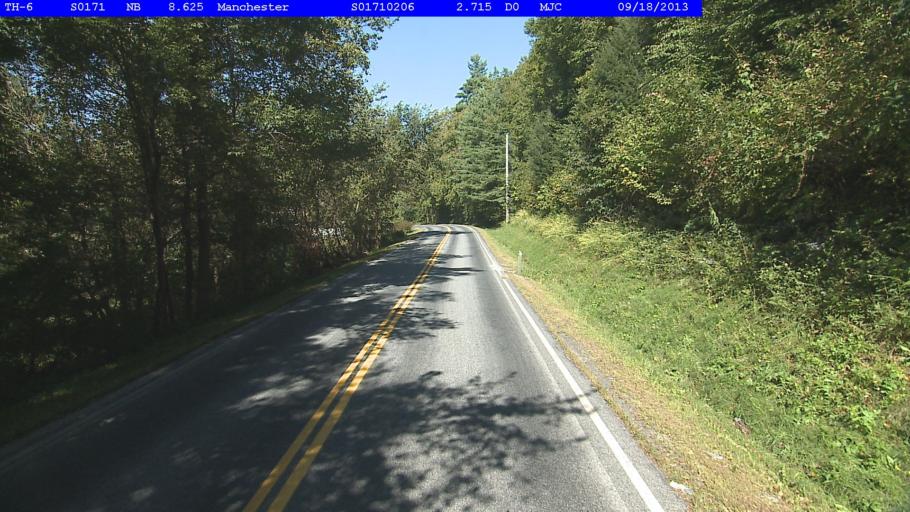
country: US
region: Vermont
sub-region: Bennington County
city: Manchester Center
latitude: 43.1442
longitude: -73.0560
